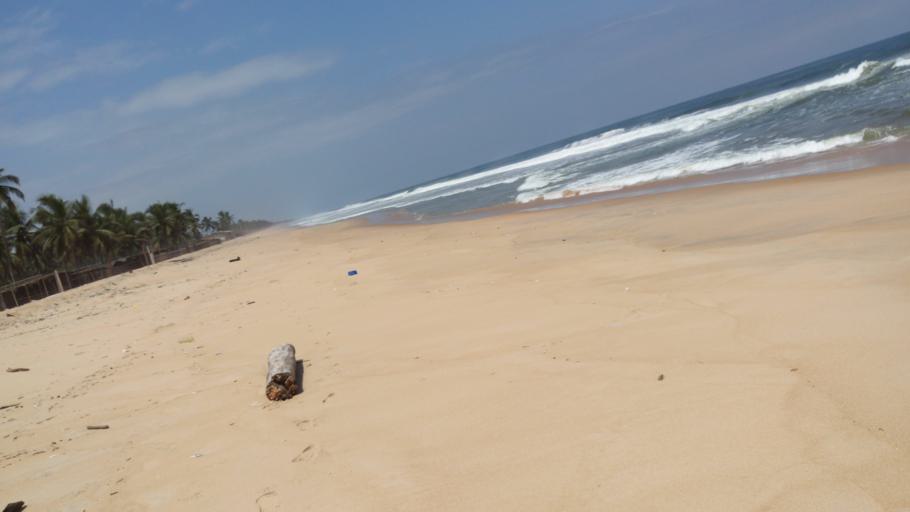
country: CI
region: Sud-Comoe
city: Grand-Bassam
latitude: 5.1870
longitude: -3.6908
